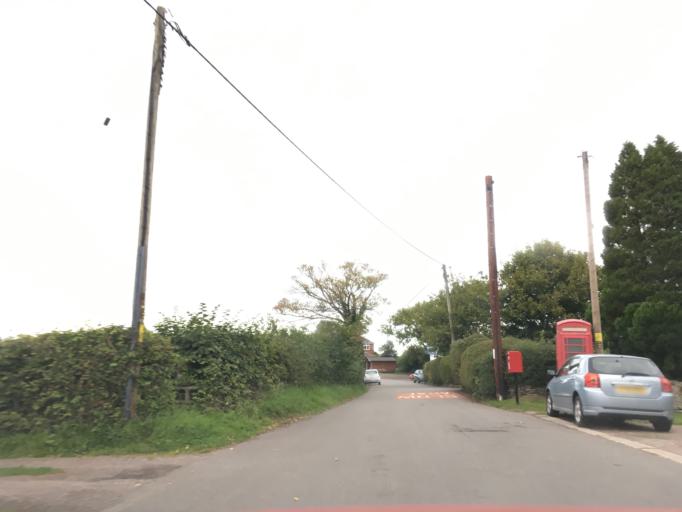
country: GB
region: Wales
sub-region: Newport
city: Caerleon
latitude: 51.6295
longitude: -2.9364
